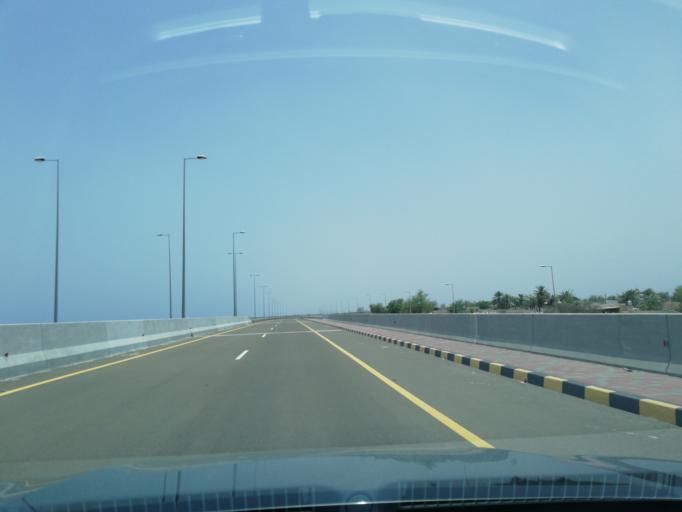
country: OM
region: Al Batinah
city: Shinas
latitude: 24.8971
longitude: 56.3980
